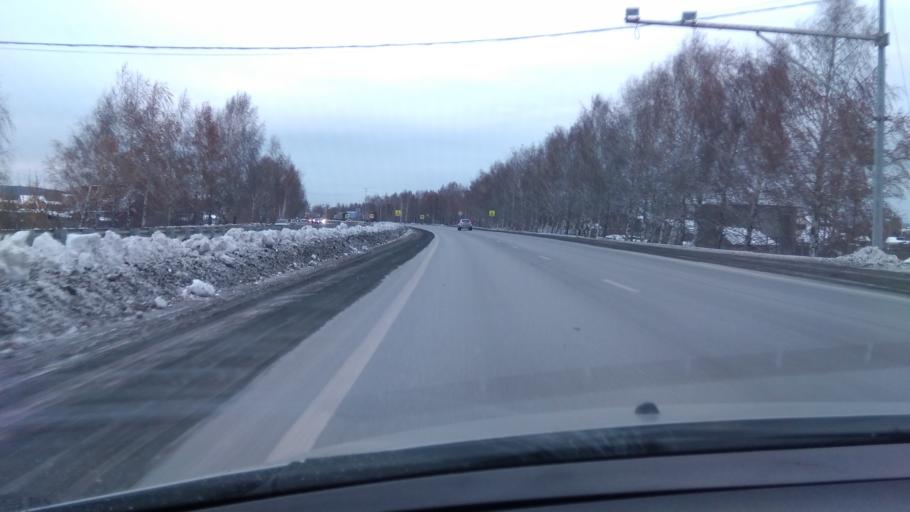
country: RU
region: Sverdlovsk
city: Aramil
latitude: 56.7014
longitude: 60.7491
